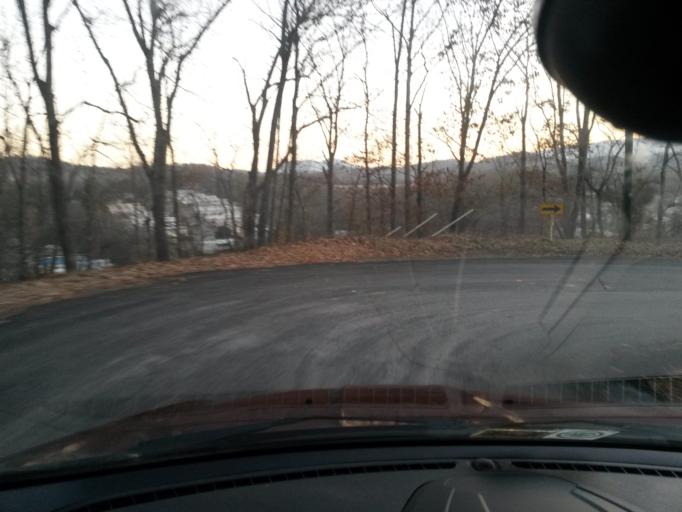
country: US
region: Virginia
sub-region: Alleghany County
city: Clifton Forge
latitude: 37.8228
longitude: -79.7997
